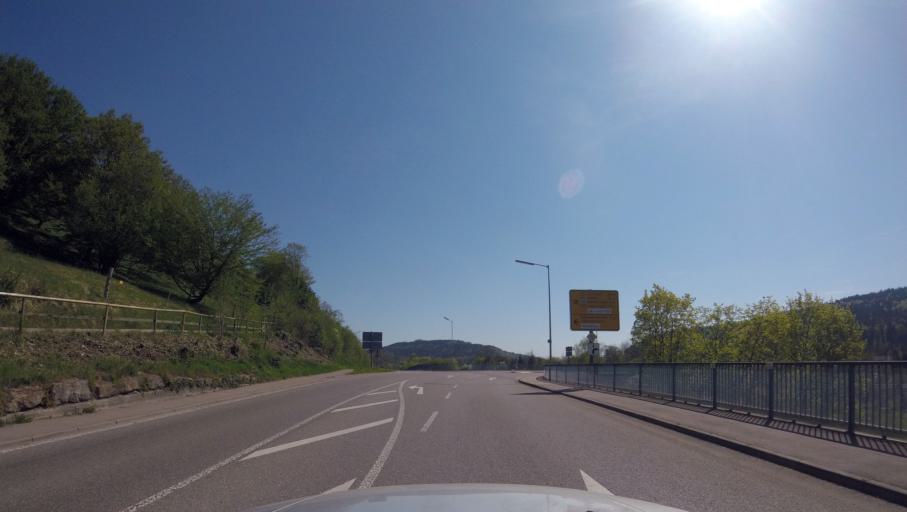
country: DE
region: Baden-Wuerttemberg
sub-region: Regierungsbezirk Stuttgart
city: Lorch
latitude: 48.7976
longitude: 9.7007
